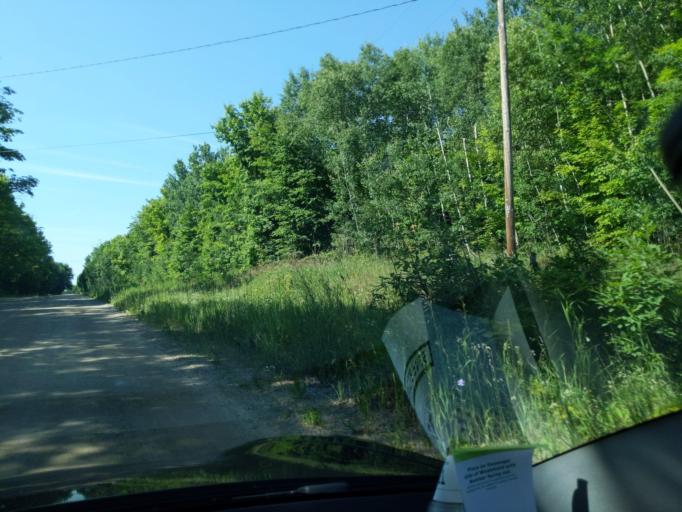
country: US
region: Michigan
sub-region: Cheboygan County
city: Cheboygan
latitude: 45.6733
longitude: -84.6508
